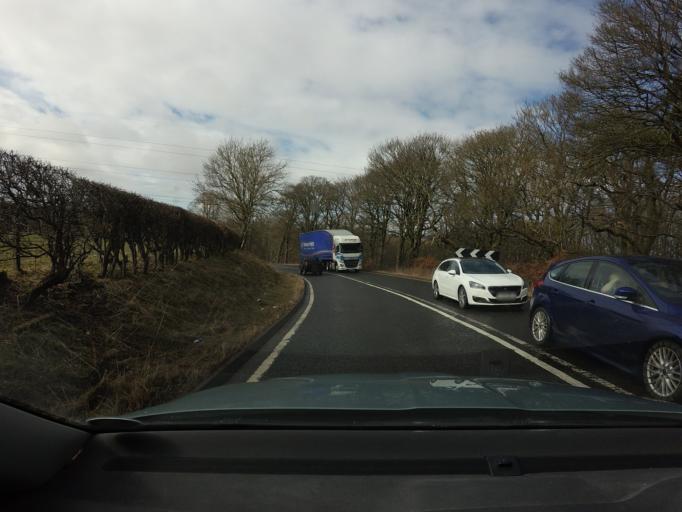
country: GB
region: Scotland
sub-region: South Lanarkshire
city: Douglas
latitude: 55.5897
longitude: -3.7988
